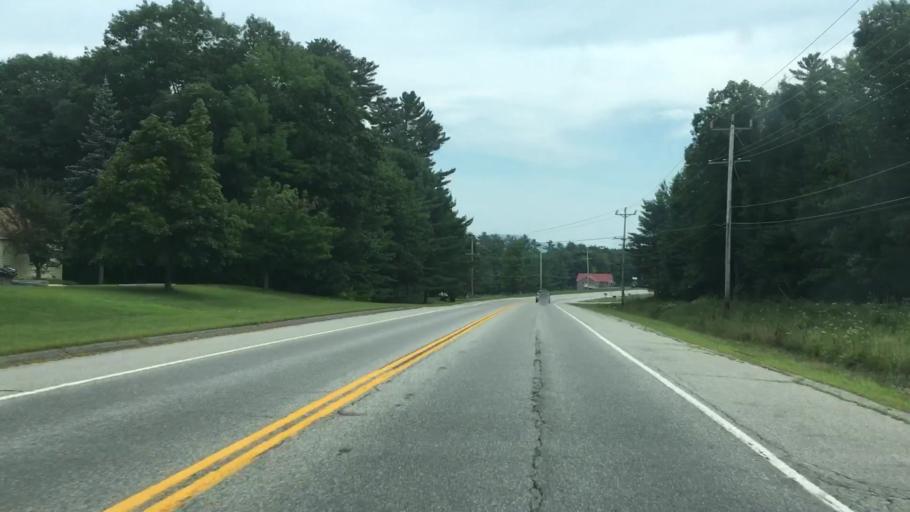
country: US
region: Maine
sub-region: Oxford County
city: Bethel
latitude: 44.4336
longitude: -70.8030
